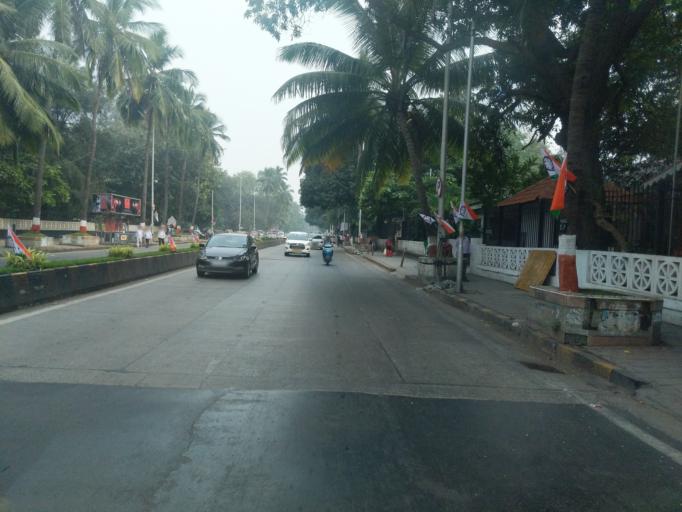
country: IN
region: Maharashtra
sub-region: Raigarh
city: Uran
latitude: 18.9287
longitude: 72.8233
